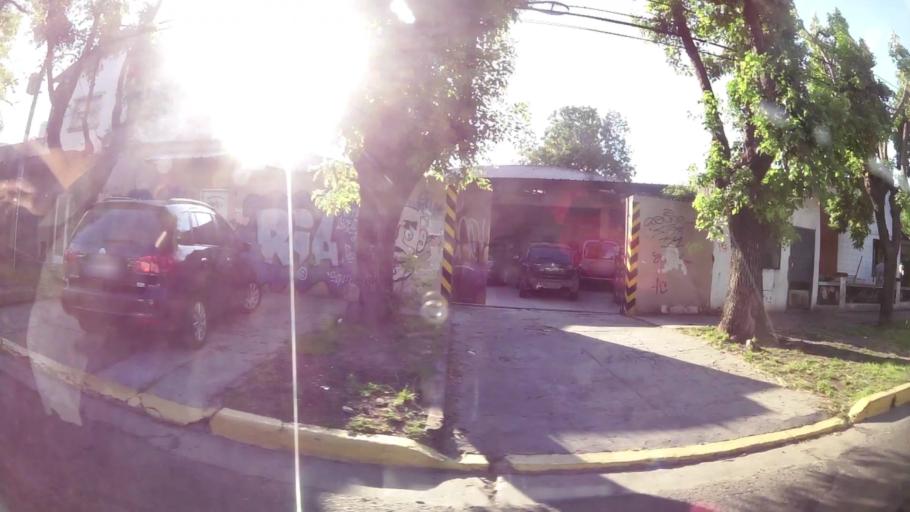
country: AR
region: Buenos Aires
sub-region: Partido de Merlo
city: Merlo
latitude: -34.6812
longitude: -58.7281
